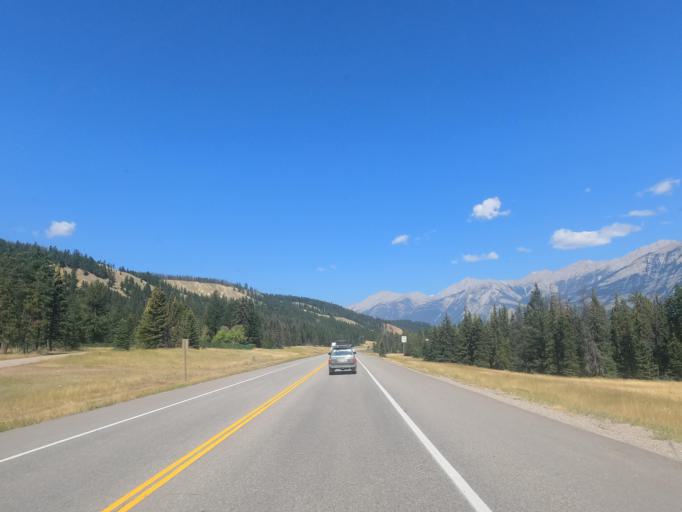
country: CA
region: Alberta
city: Jasper Park Lodge
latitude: 52.8994
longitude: -118.0663
